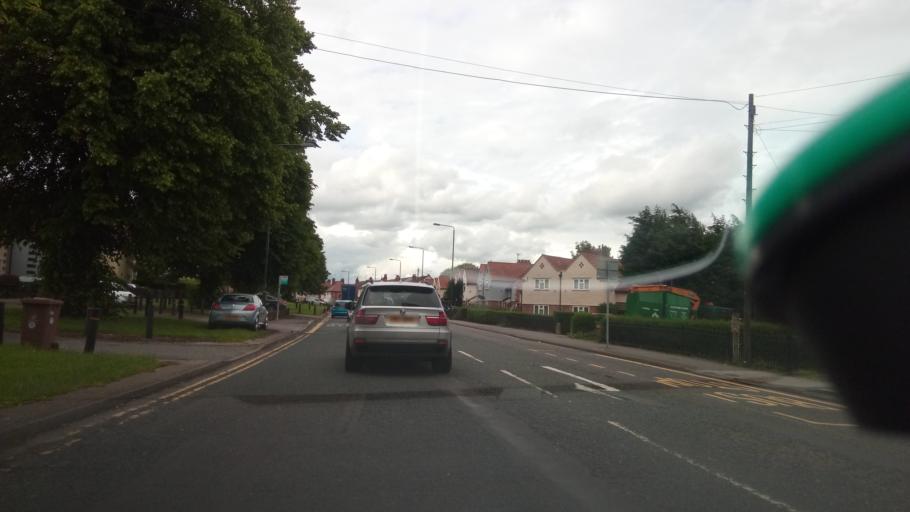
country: GB
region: England
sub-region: Derby
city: Derby
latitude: 52.8935
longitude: -1.4588
